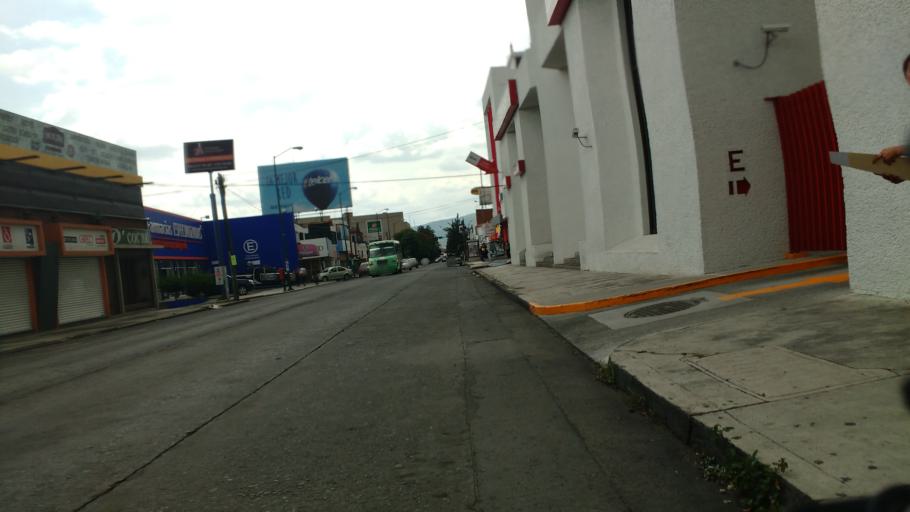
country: MX
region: Michoacan
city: Morelia
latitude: 19.6942
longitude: -101.1824
